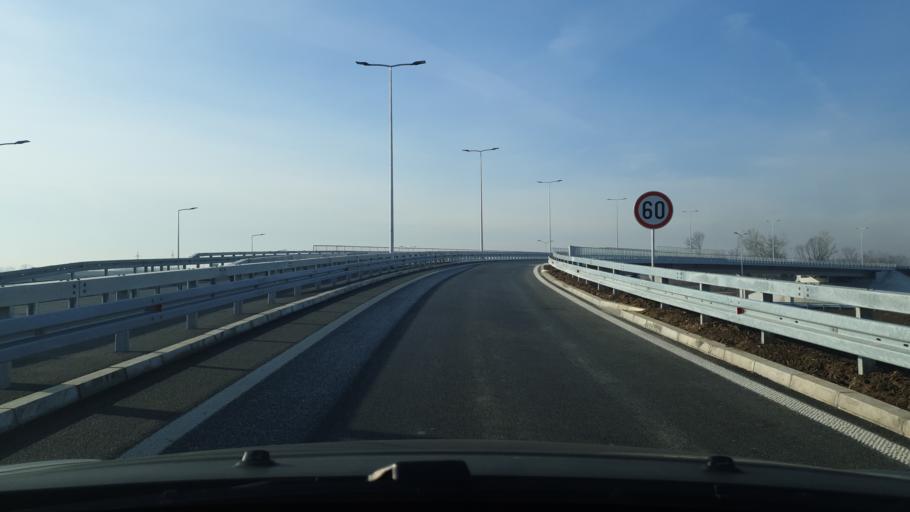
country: RS
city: Baric
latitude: 44.6514
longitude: 20.2329
